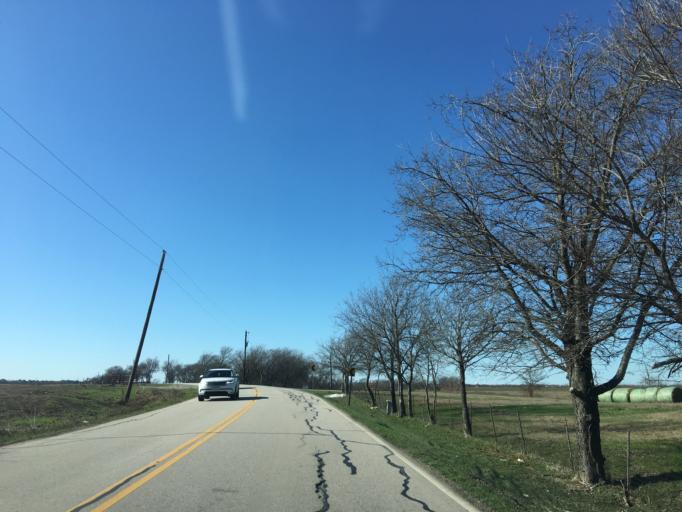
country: US
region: Texas
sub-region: Collin County
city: Prosper
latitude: 33.2337
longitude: -96.8323
